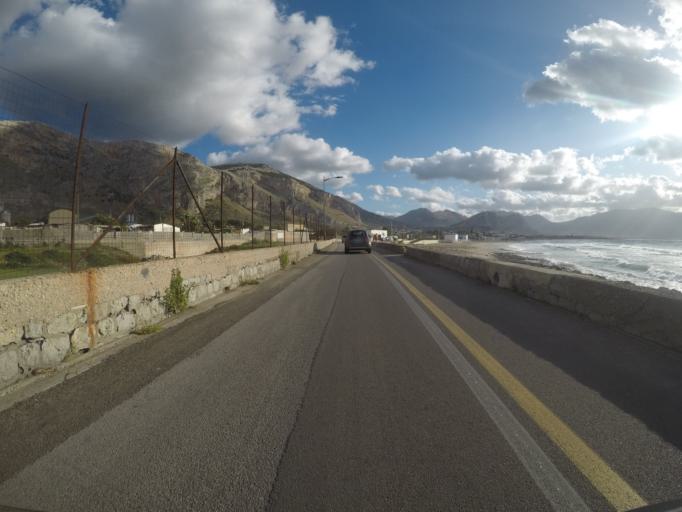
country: IT
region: Sicily
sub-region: Palermo
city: Isola delle Femmine
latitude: 38.1933
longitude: 13.2443
